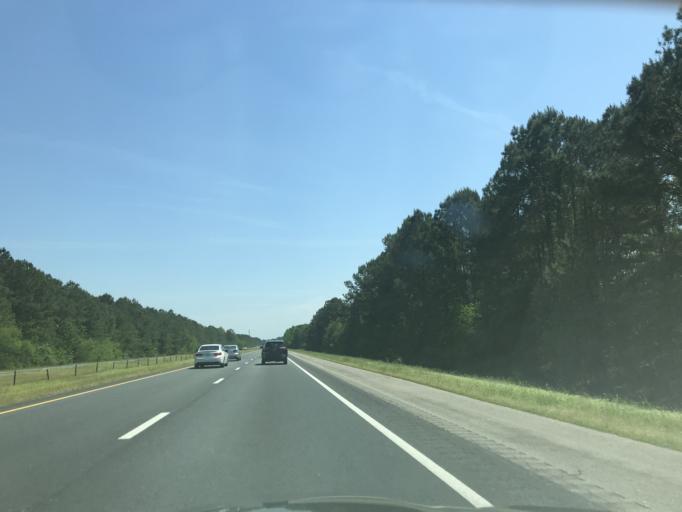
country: US
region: North Carolina
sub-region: Johnston County
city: Benson
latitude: 35.3622
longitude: -78.4888
